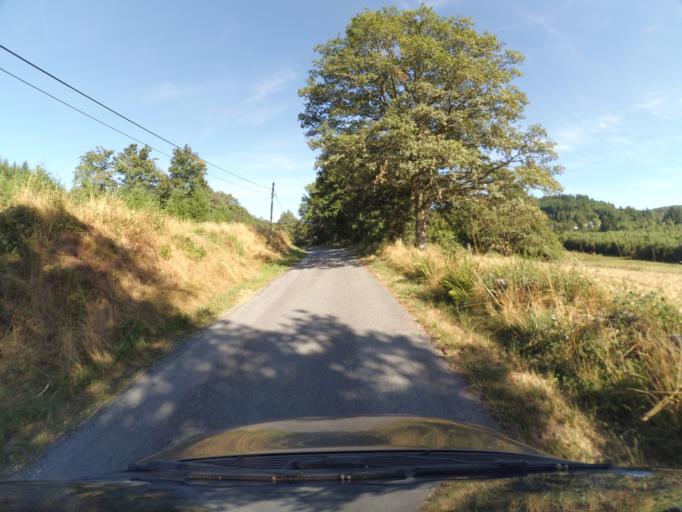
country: FR
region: Limousin
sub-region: Departement de la Correze
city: Bugeat
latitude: 45.6827
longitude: 1.9413
